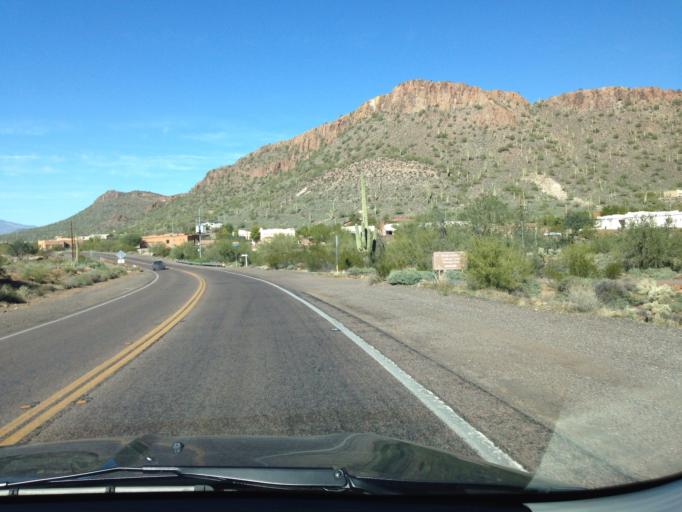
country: US
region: Arizona
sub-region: Maricopa County
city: Anthem
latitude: 33.8635
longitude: -112.0582
